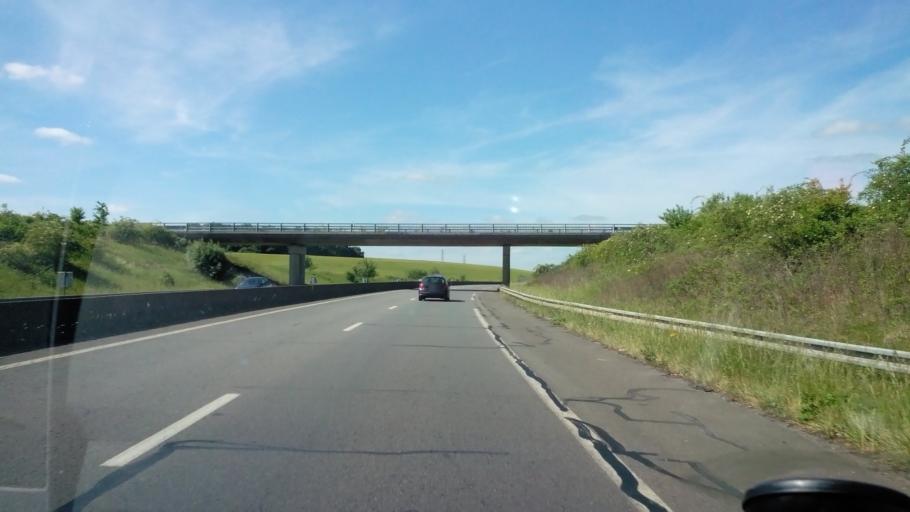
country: FR
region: Lorraine
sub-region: Departement de la Moselle
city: Peltre
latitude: 49.0678
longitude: 6.2041
